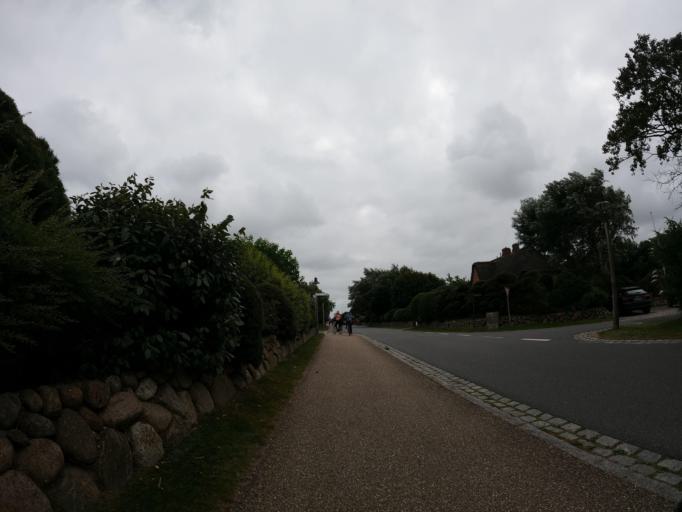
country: DE
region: Schleswig-Holstein
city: Tinnum
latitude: 54.9513
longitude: 8.3445
